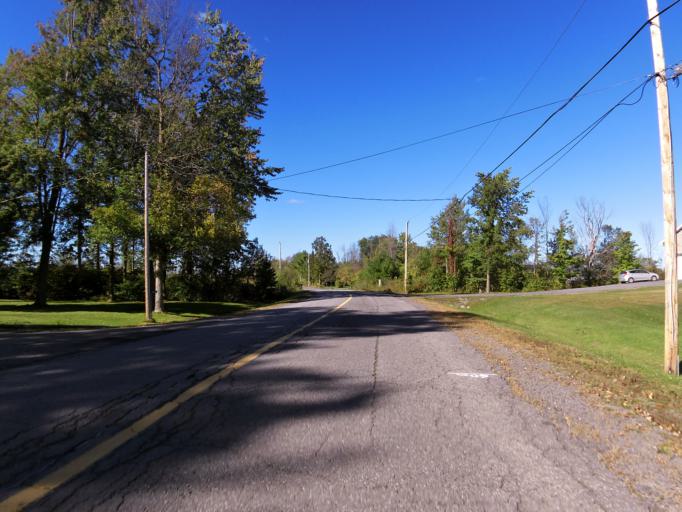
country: CA
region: Ontario
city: Clarence-Rockland
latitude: 45.4017
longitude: -75.3680
